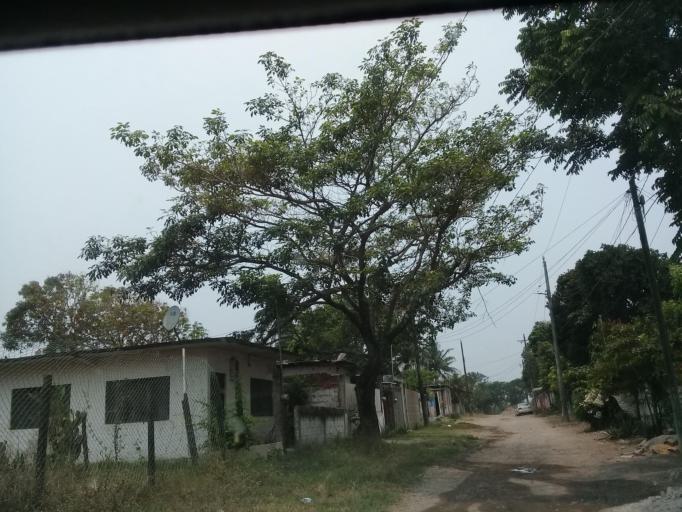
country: MX
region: Veracruz
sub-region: Veracruz
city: Las Amapolas
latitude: 19.1408
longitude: -96.2079
